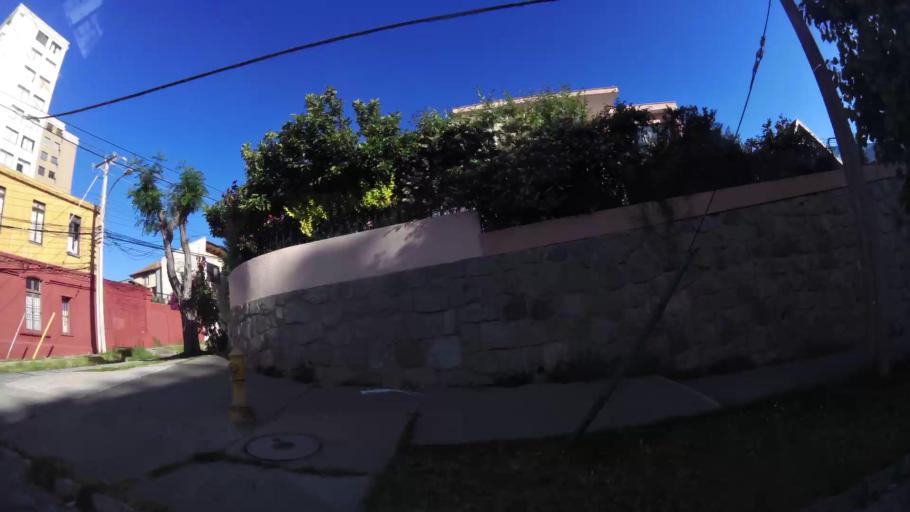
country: CL
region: Valparaiso
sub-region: Provincia de Valparaiso
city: Vina del Mar
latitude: -33.0286
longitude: -71.5719
